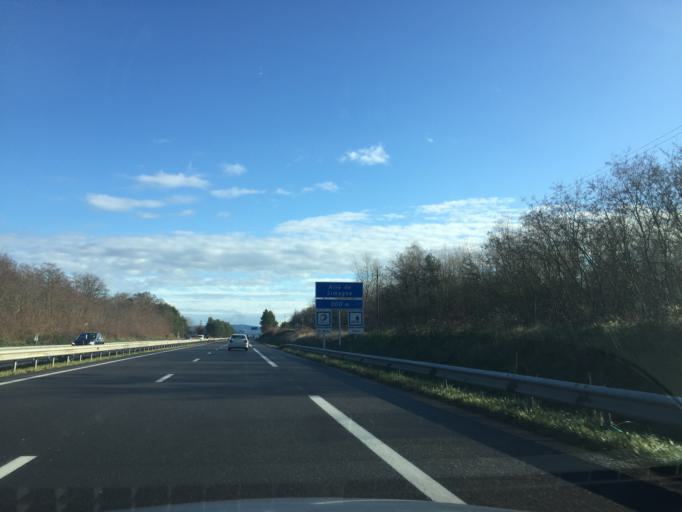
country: FR
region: Auvergne
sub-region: Departement du Puy-de-Dome
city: Orleat
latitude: 45.8523
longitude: 3.3953
